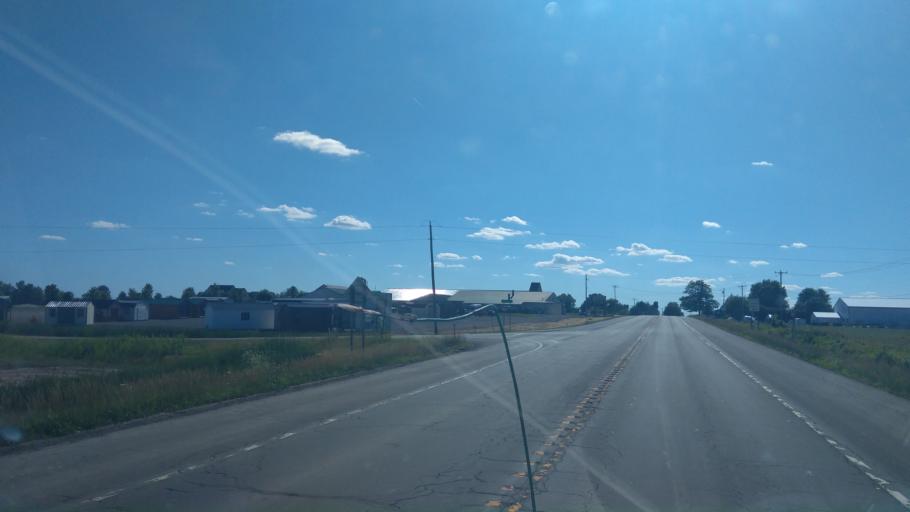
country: US
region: New York
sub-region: Seneca County
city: Waterloo
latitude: 42.9550
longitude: -76.8862
